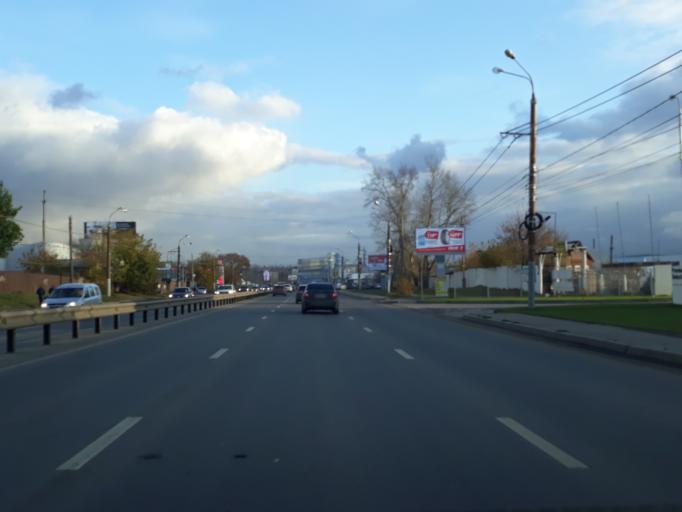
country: RU
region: Nizjnij Novgorod
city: Nizhniy Novgorod
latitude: 56.2999
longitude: 43.9241
